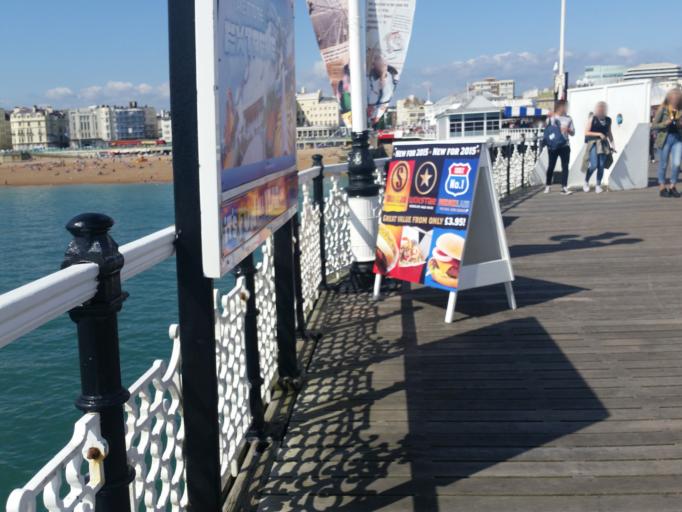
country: GB
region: England
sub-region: Brighton and Hove
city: Brighton
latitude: 50.8166
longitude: -0.1370
